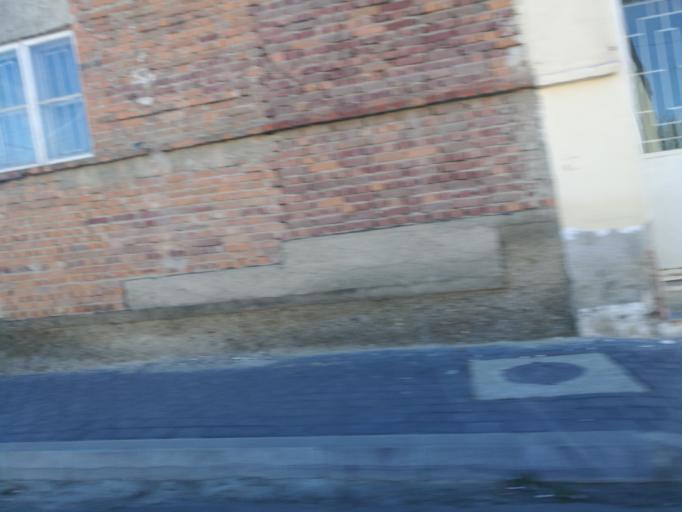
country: RO
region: Brasov
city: Fogarasch
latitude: 45.8406
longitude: 24.9733
